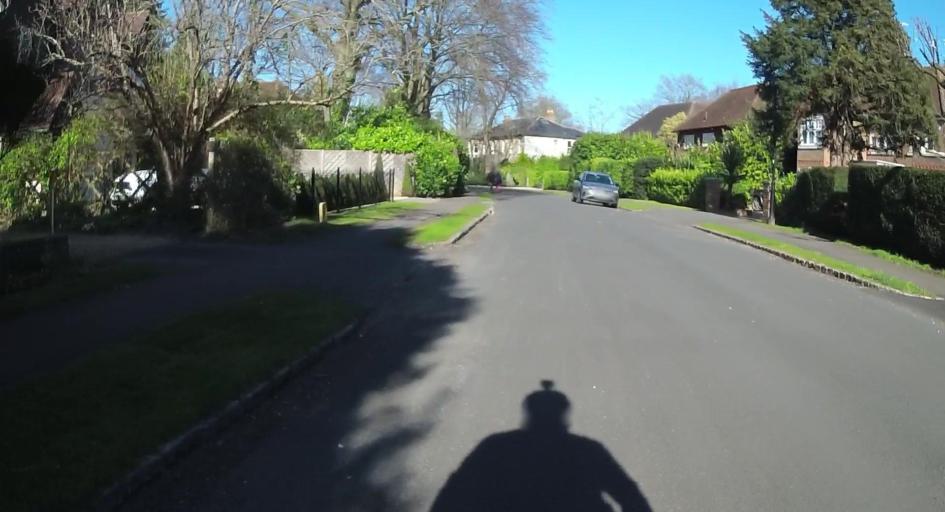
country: GB
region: England
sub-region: Surrey
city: Weybridge
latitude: 51.3703
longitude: -0.4438
